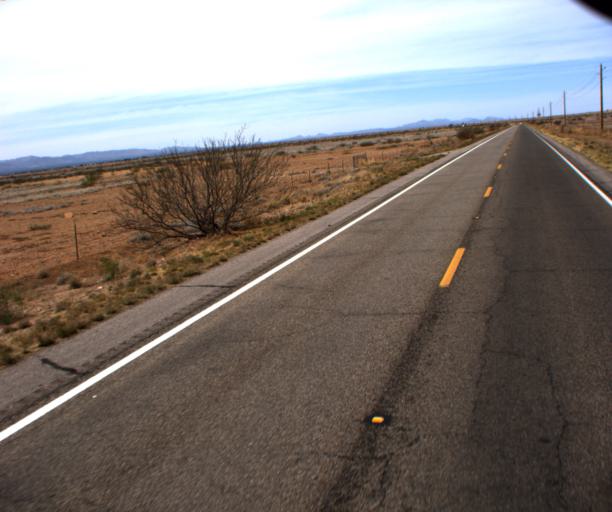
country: US
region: Arizona
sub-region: Cochise County
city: Pirtleville
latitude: 31.4274
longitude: -109.5841
